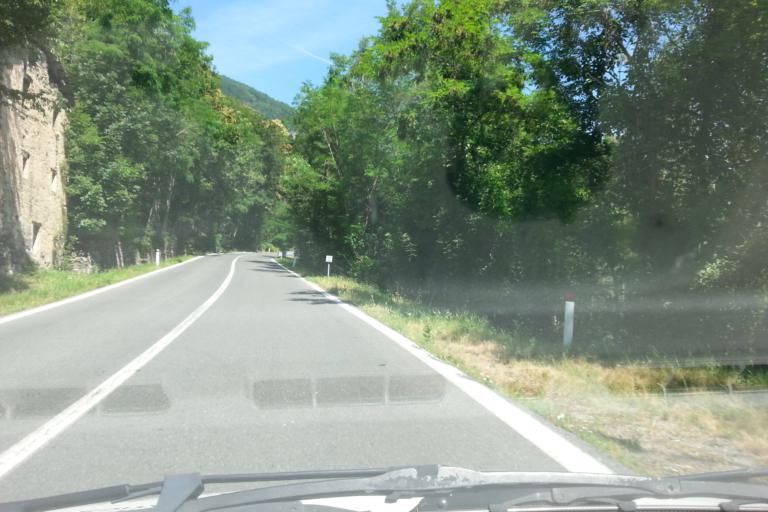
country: IT
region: Piedmont
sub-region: Provincia di Torino
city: Venaus
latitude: 45.1495
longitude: 6.9997
